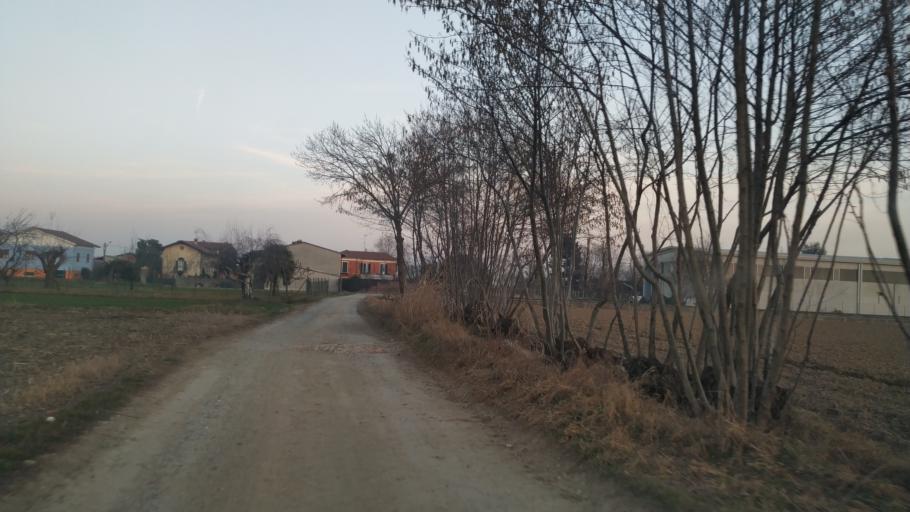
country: IT
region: Piedmont
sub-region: Provincia di Vercelli
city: Cigliano
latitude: 45.3030
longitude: 8.0203
